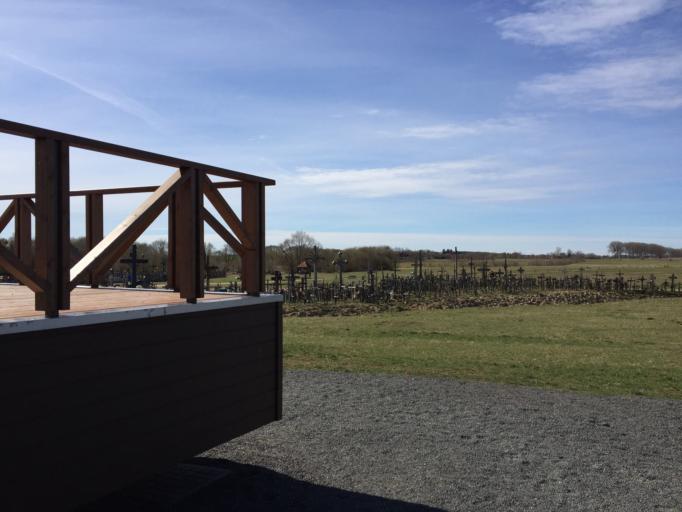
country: LT
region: Siauliu apskritis
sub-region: Siauliai
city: Siauliai
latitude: 56.0159
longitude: 23.4155
